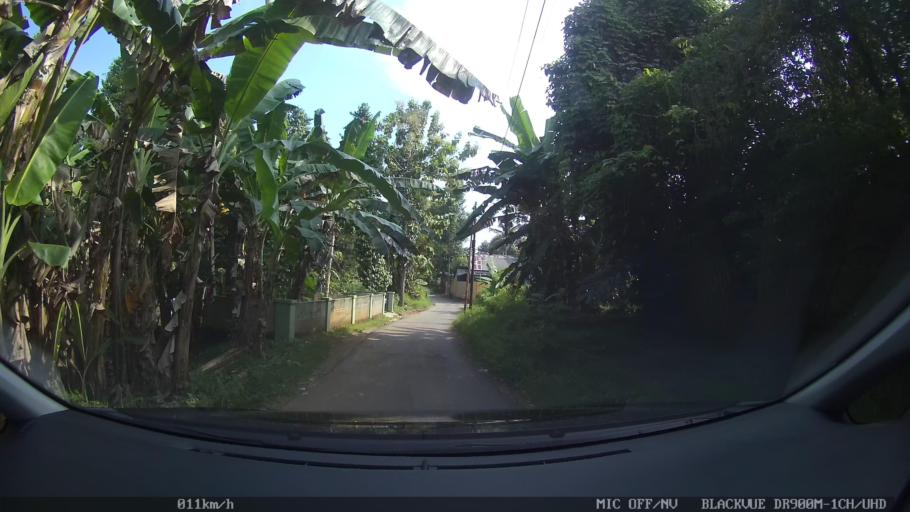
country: ID
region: Lampung
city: Kedaton
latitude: -5.3861
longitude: 105.2236
